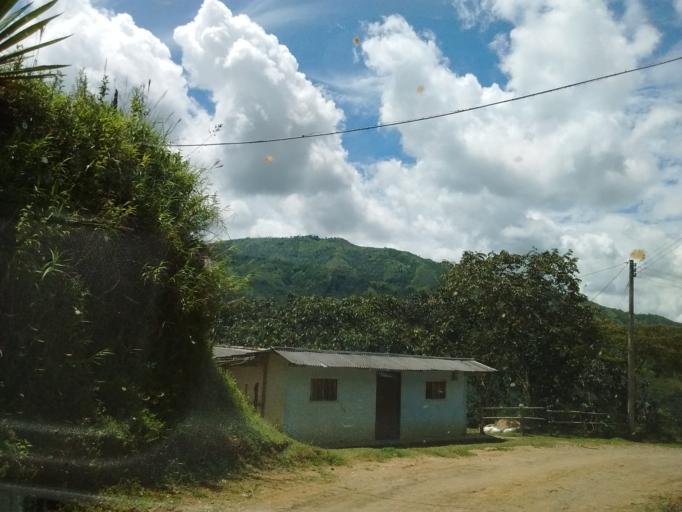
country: CO
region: Cauca
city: Villa Rica
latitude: 2.6495
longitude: -76.7687
